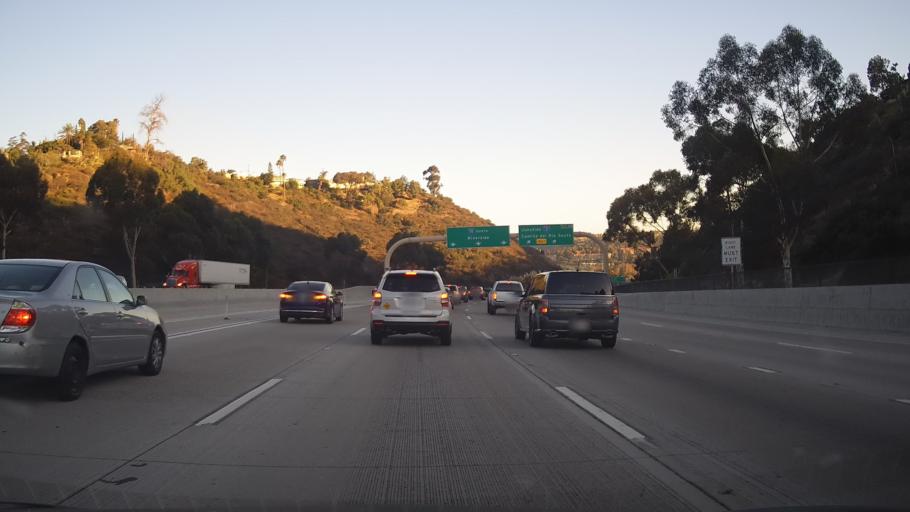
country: US
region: California
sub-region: San Diego County
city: San Diego
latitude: 32.7711
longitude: -117.1121
